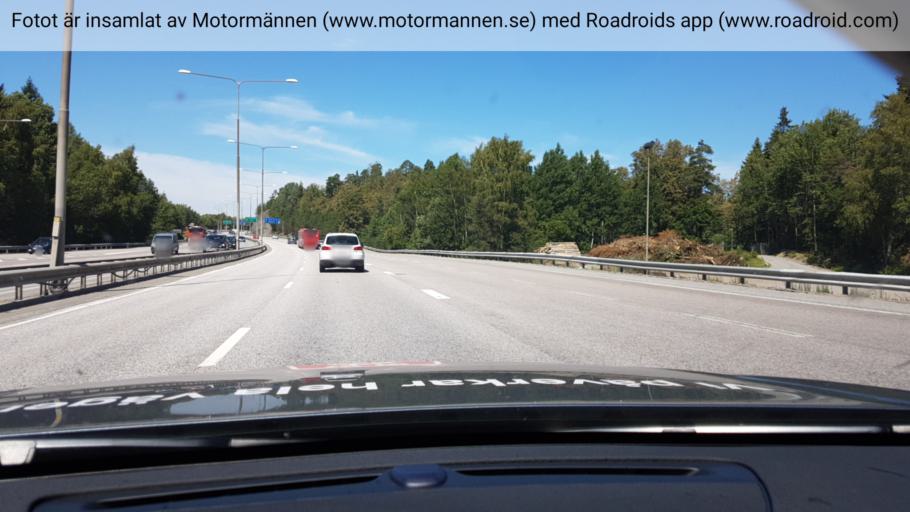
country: SE
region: Stockholm
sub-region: Haninge Kommun
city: Handen
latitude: 59.2218
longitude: 18.1330
